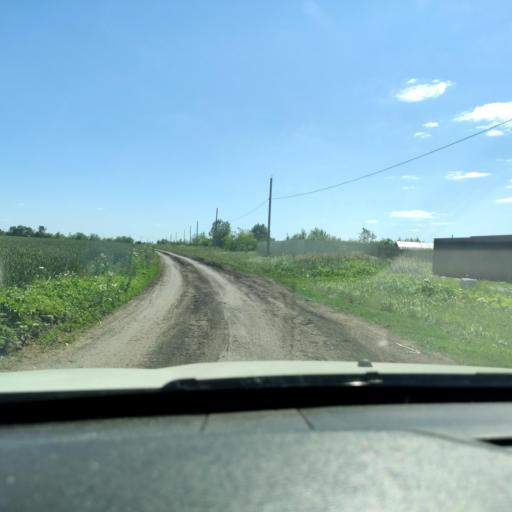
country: RU
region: Samara
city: Dubovyy Umet
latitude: 53.0266
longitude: 50.2525
